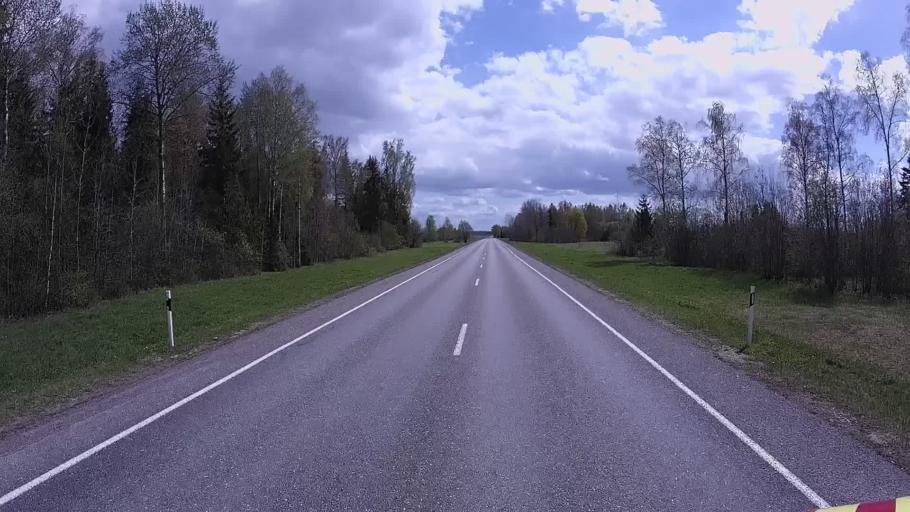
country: EE
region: Jaervamaa
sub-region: Jaerva-Jaani vald
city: Jarva-Jaani
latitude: 59.1283
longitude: 25.7813
